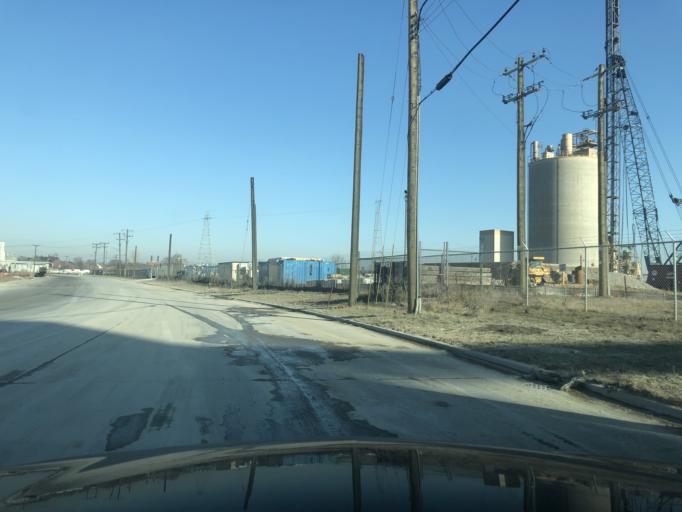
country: US
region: Michigan
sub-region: Wayne County
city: River Rouge
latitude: 42.2909
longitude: -83.1043
